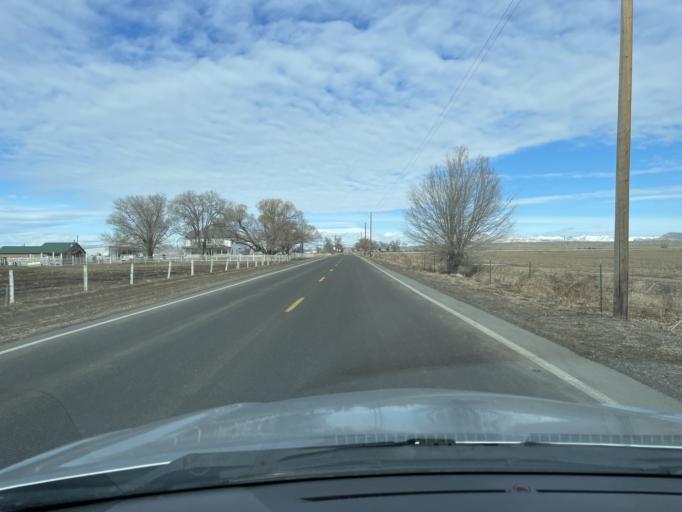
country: US
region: Colorado
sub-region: Mesa County
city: Loma
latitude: 39.2483
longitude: -108.8129
